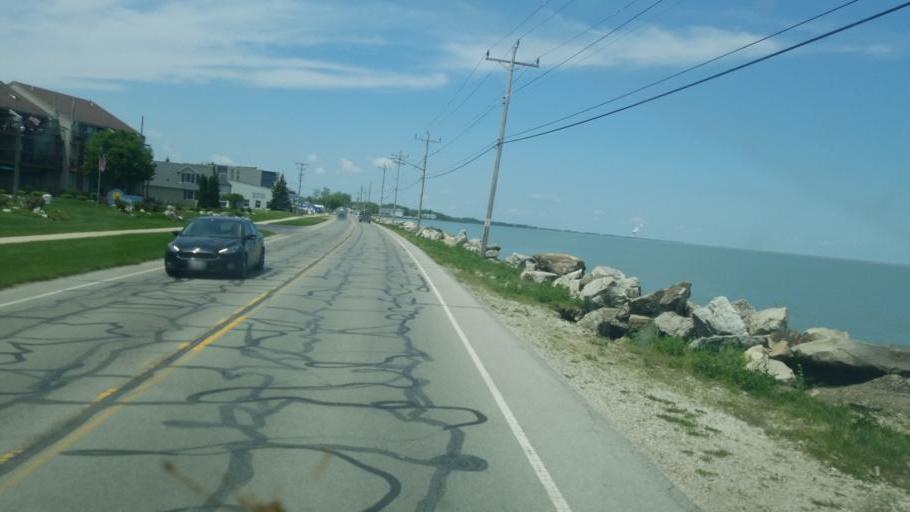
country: US
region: Ohio
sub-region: Ottawa County
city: Port Clinton
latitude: 41.5188
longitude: -82.9493
